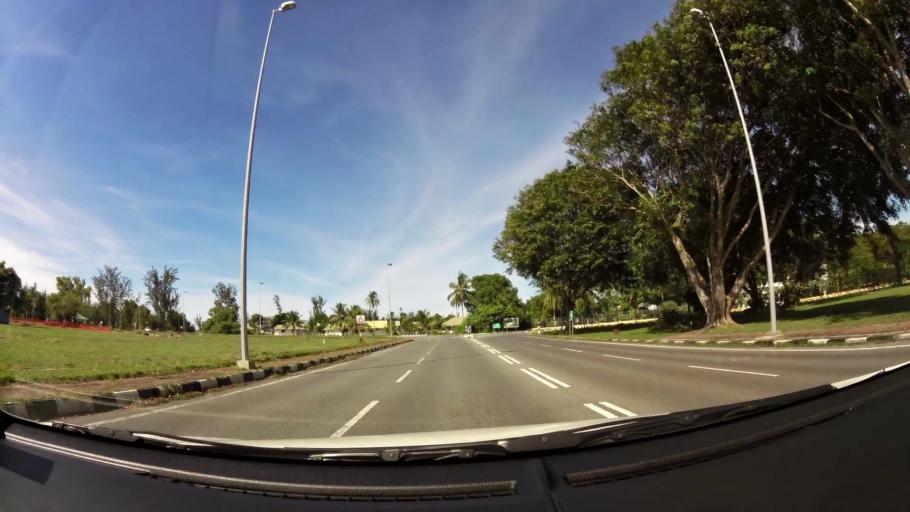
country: BN
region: Belait
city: Kuala Belait
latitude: 4.5865
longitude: 114.2017
